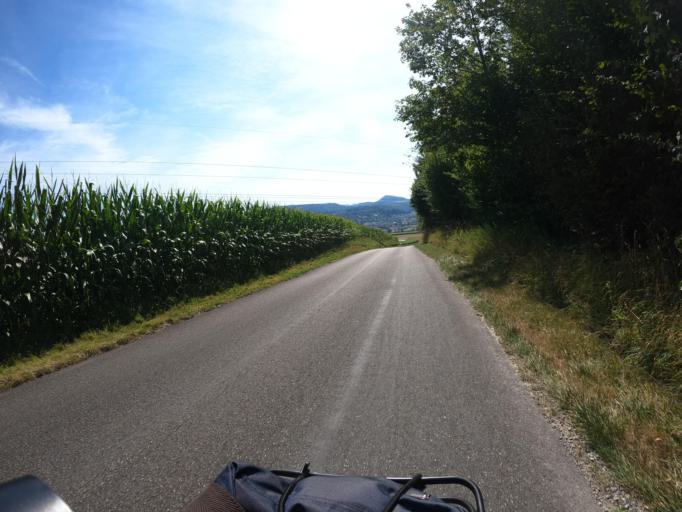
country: CH
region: Zurich
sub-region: Bezirk Affoltern
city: Hedingen
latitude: 47.3057
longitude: 8.4300
